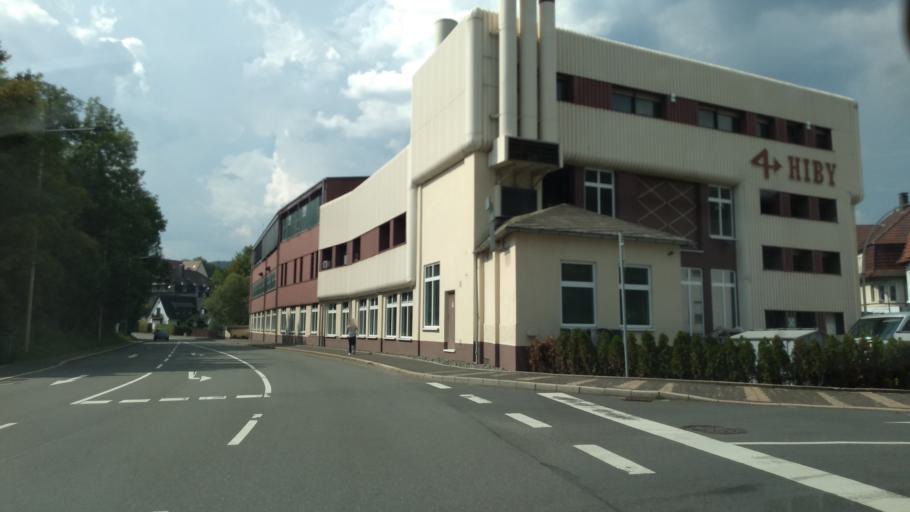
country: DE
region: North Rhine-Westphalia
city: Plettenberg
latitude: 51.2111
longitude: 7.8805
